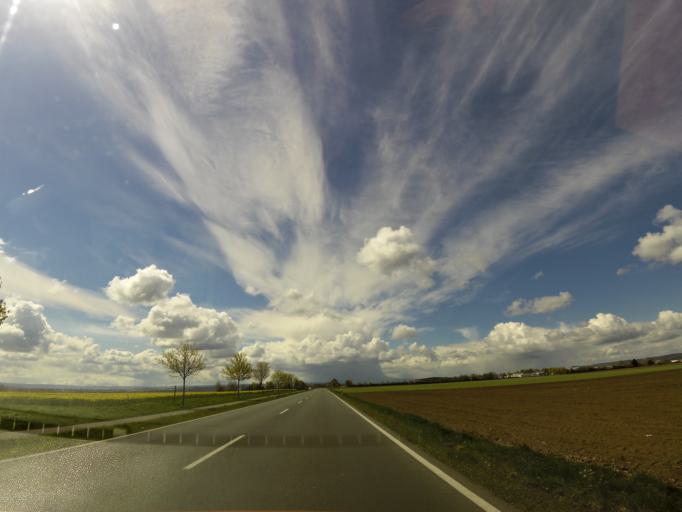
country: DE
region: Saxony-Anhalt
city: Gross Quenstedt
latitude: 51.9225
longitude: 11.1556
